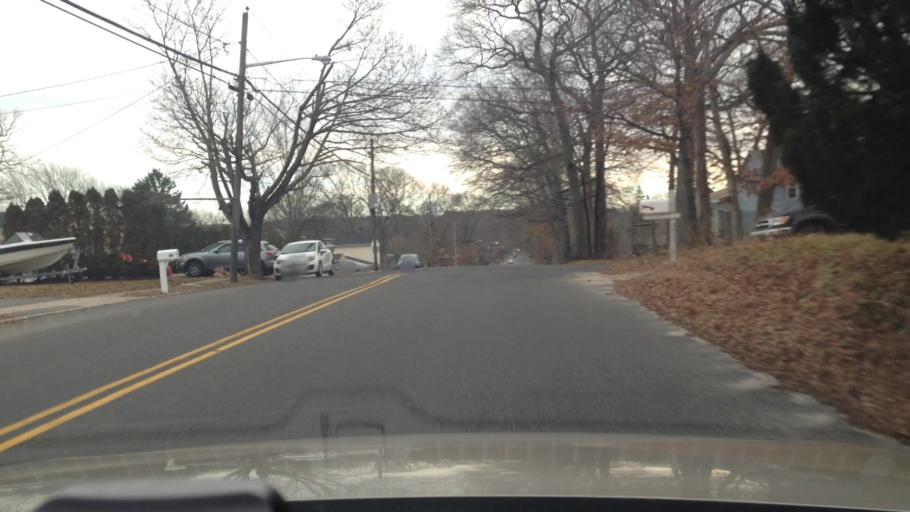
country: US
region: New York
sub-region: Suffolk County
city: Selden
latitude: 40.8619
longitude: -73.0346
